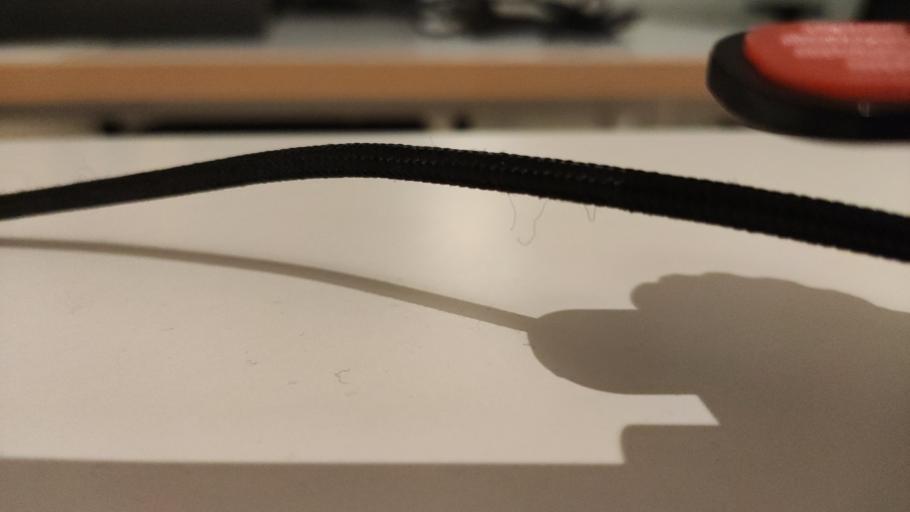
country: RU
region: Moskovskaya
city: Kurovskoye
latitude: 55.5366
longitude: 38.8728
